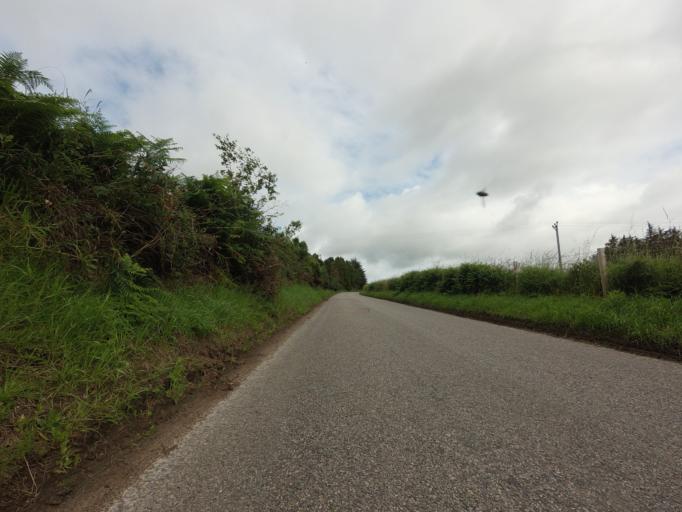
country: GB
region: Scotland
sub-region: Moray
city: Elgin
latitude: 57.6585
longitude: -3.3535
